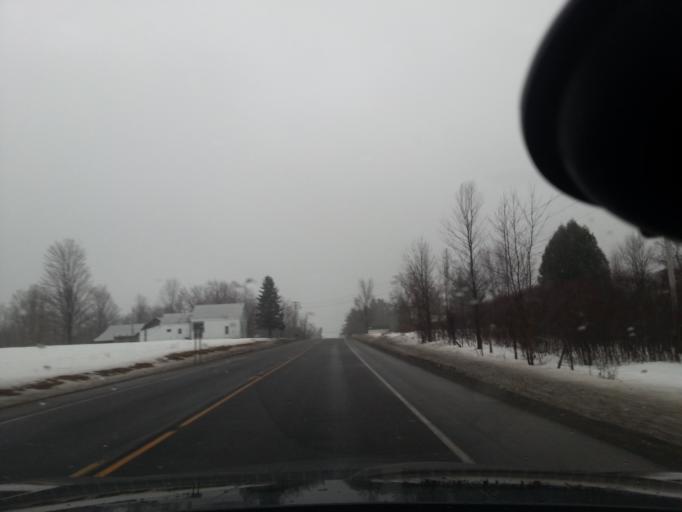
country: US
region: New York
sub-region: St. Lawrence County
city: Ogdensburg
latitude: 44.6007
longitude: -75.3874
